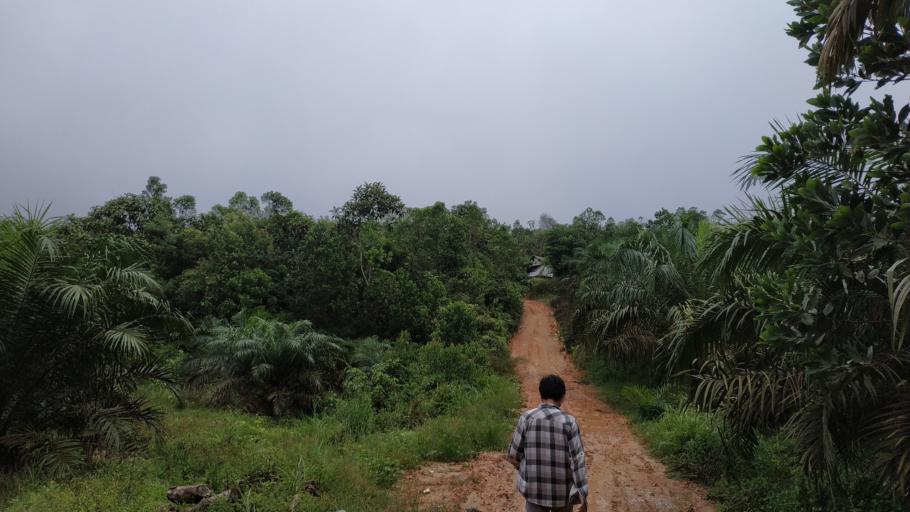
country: ID
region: Riau
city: Pekanbaru
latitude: 0.4853
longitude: 101.5649
